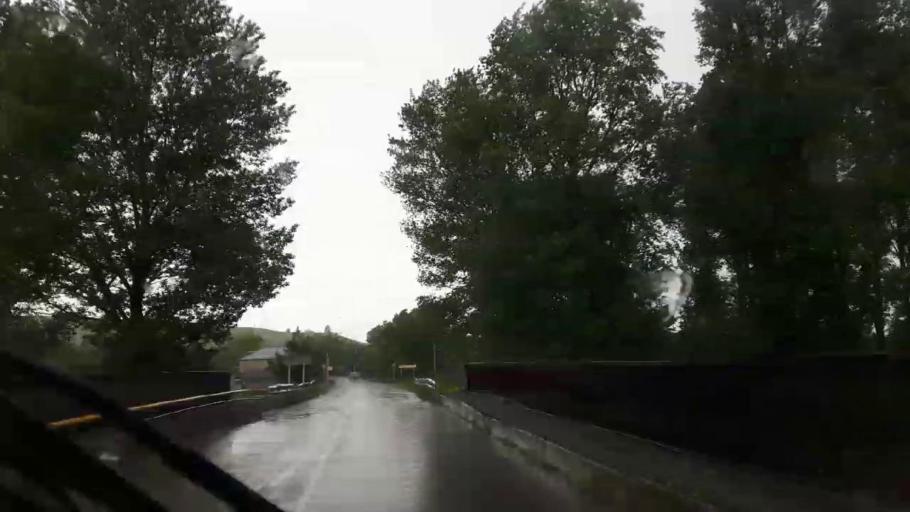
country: GE
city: Agara
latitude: 42.0126
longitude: 43.8527
